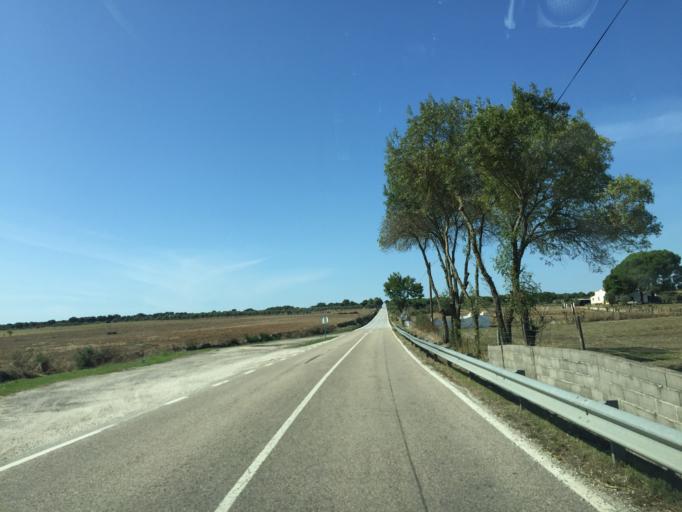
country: PT
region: Portalegre
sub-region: Portalegre
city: Alagoa
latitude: 39.4261
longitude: -7.5885
